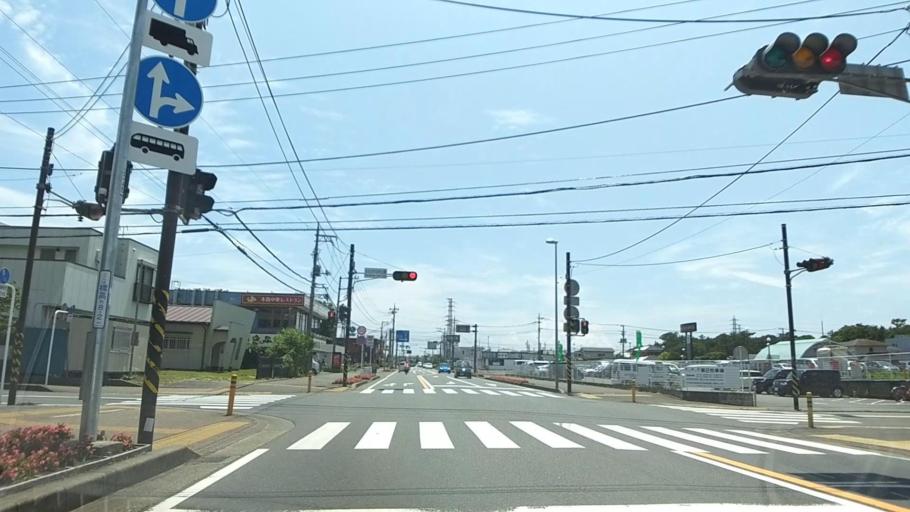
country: JP
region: Kanagawa
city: Chigasaki
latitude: 35.3737
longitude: 139.3835
